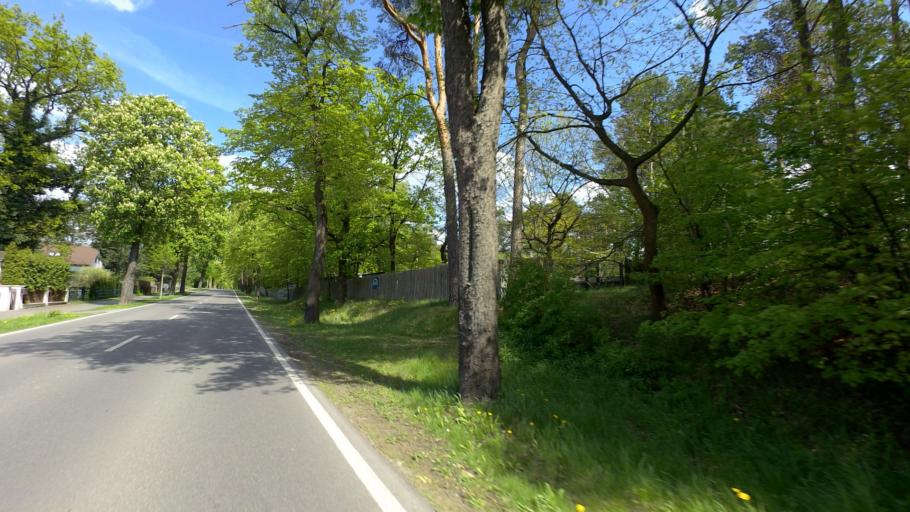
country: DE
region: Brandenburg
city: Wandlitz
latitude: 52.8013
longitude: 13.4842
